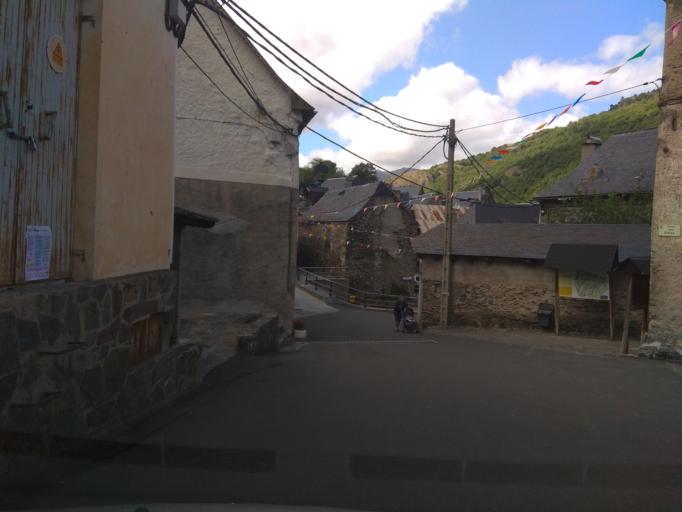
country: ES
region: Catalonia
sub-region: Provincia de Lleida
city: Les
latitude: 42.7376
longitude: 0.7193
